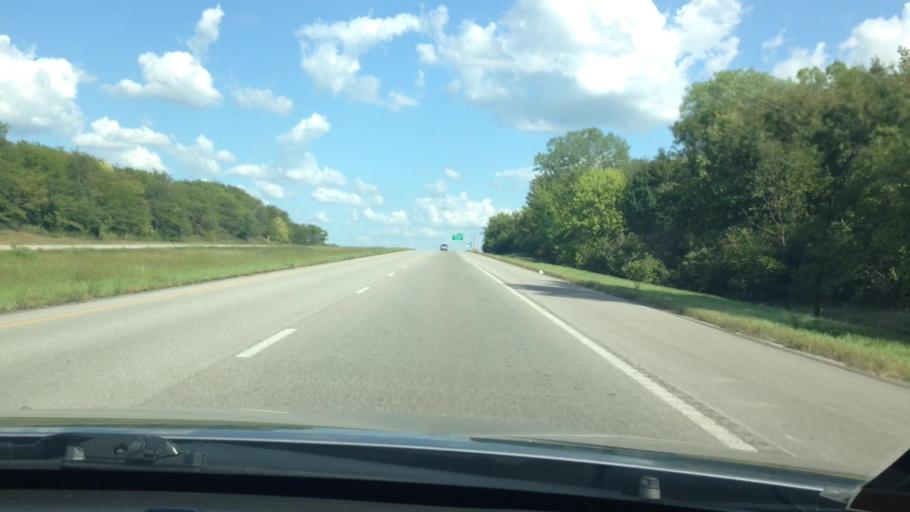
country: US
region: Missouri
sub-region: Clay County
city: Smithville
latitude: 39.3111
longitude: -94.5647
